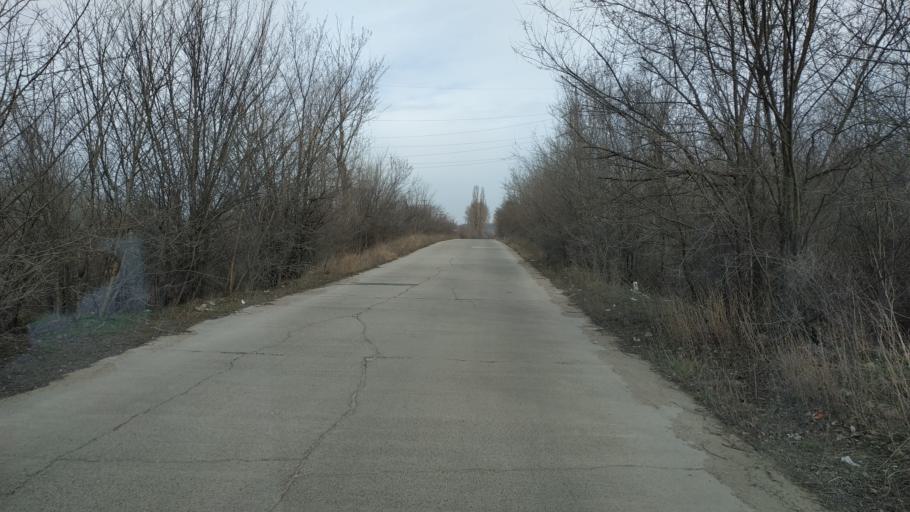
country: MD
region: Chisinau
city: Vatra
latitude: 47.0855
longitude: 28.7408
